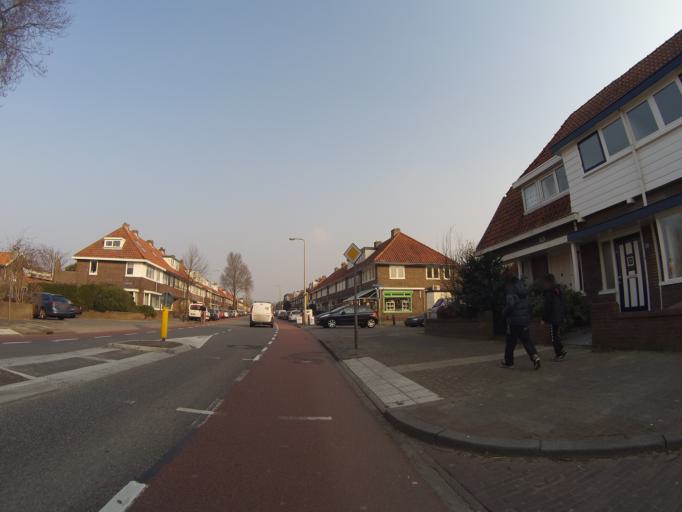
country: NL
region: Utrecht
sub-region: Gemeente Amersfoort
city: Hoogland
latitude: 52.1608
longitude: 5.3601
